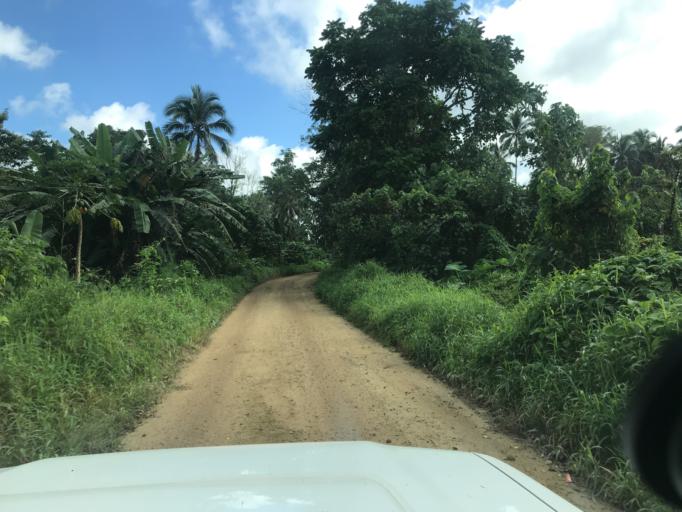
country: VU
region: Sanma
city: Luganville
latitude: -15.4783
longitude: 167.0876
